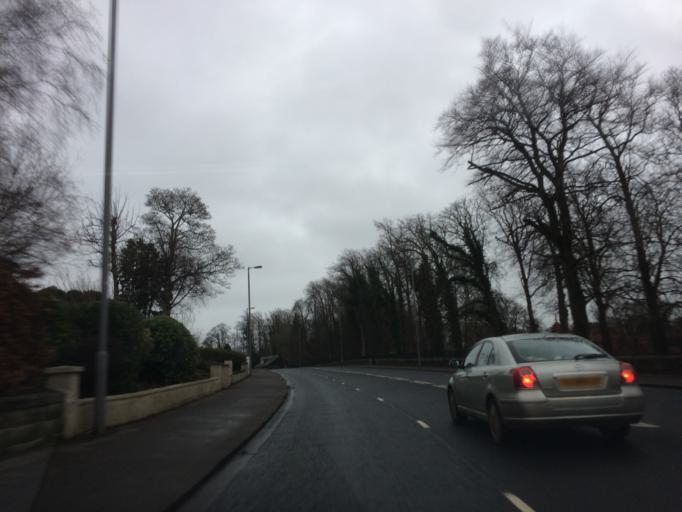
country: GB
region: Scotland
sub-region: East Renfrewshire
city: Giffnock
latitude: 55.7989
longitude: -4.3148
